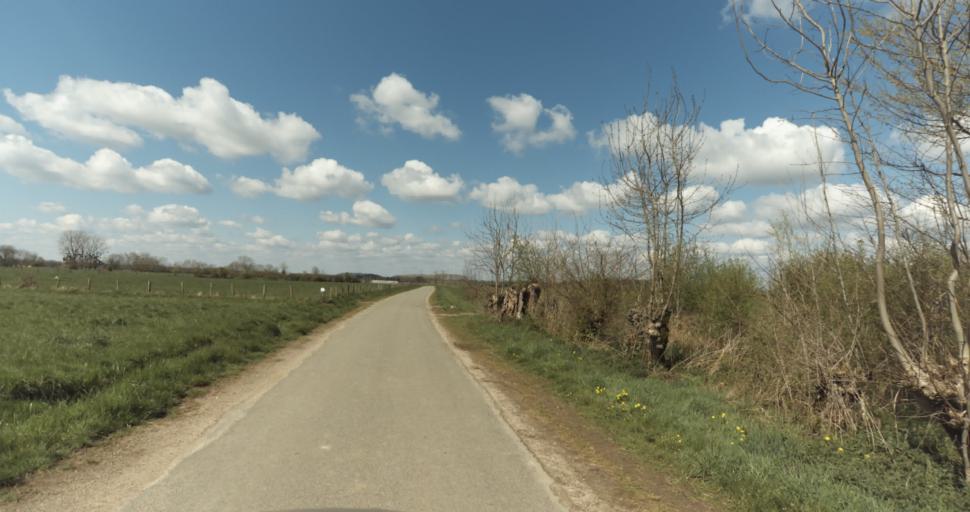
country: FR
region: Bourgogne
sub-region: Departement de la Cote-d'Or
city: Auxonne
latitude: 47.2109
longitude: 5.4106
